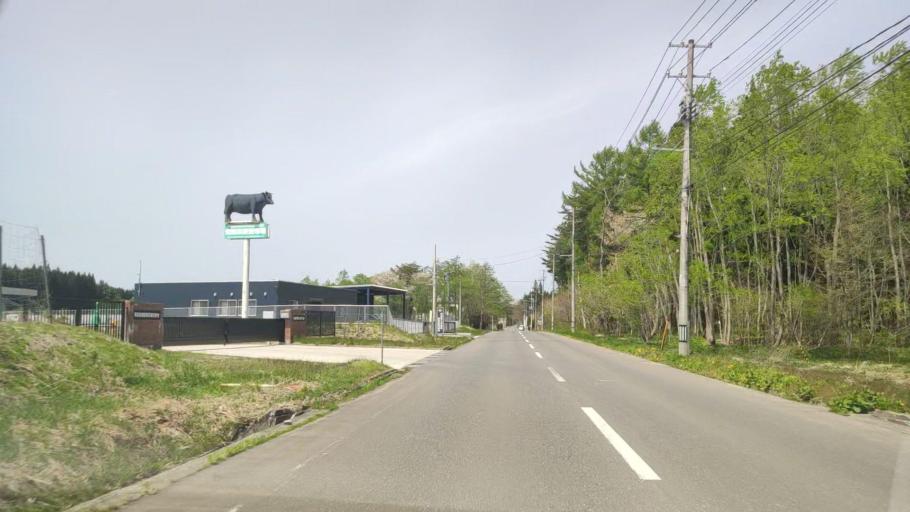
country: JP
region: Aomori
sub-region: Misawa Shi
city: Inuotose
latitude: 40.7177
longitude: 141.1430
